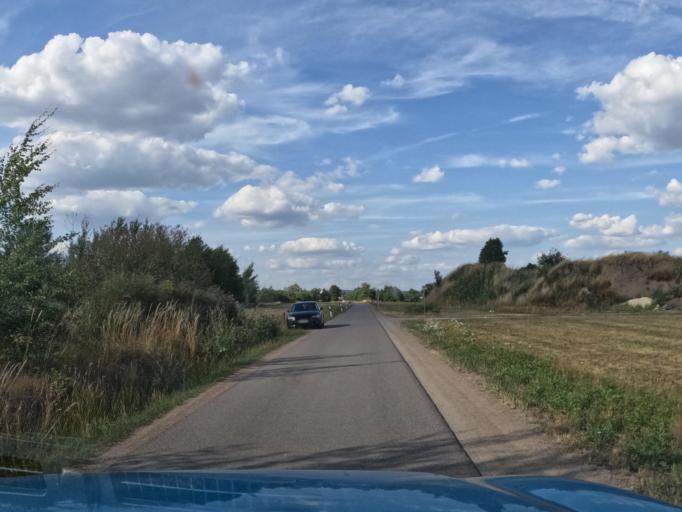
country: DE
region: Bavaria
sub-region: Upper Palatinate
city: Schwarzenfeld
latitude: 49.3759
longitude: 12.1186
